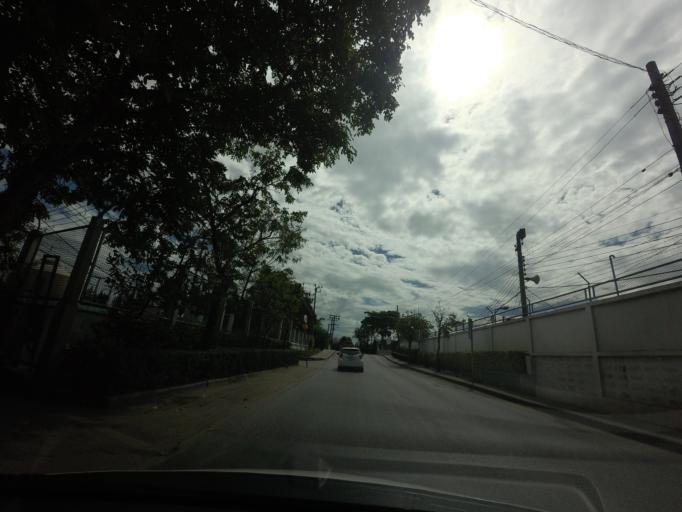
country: TH
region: Bangkok
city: Phra Khanong
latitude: 13.6897
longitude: 100.5905
